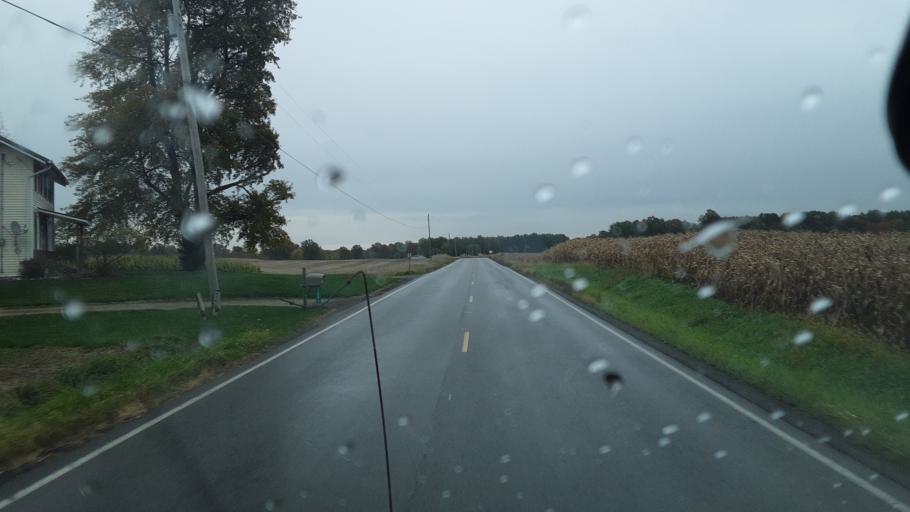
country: US
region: Ohio
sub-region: Wayne County
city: West Salem
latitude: 40.9278
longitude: -82.0666
